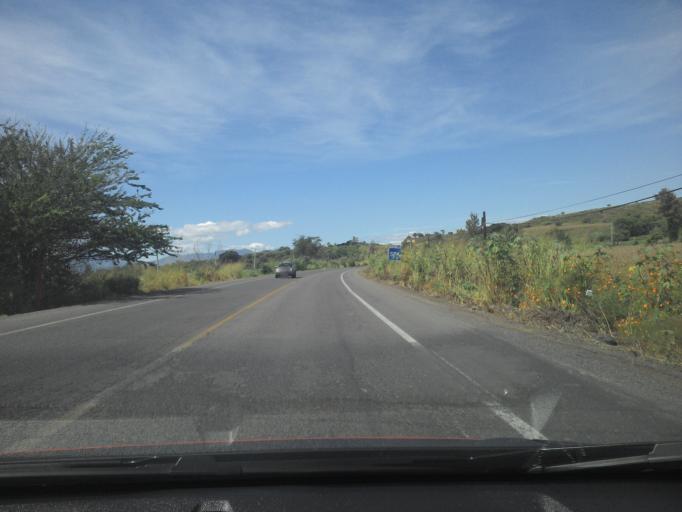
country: MX
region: Jalisco
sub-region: Teuchitlan
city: La Estanzuela
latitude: 20.6744
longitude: -103.8302
